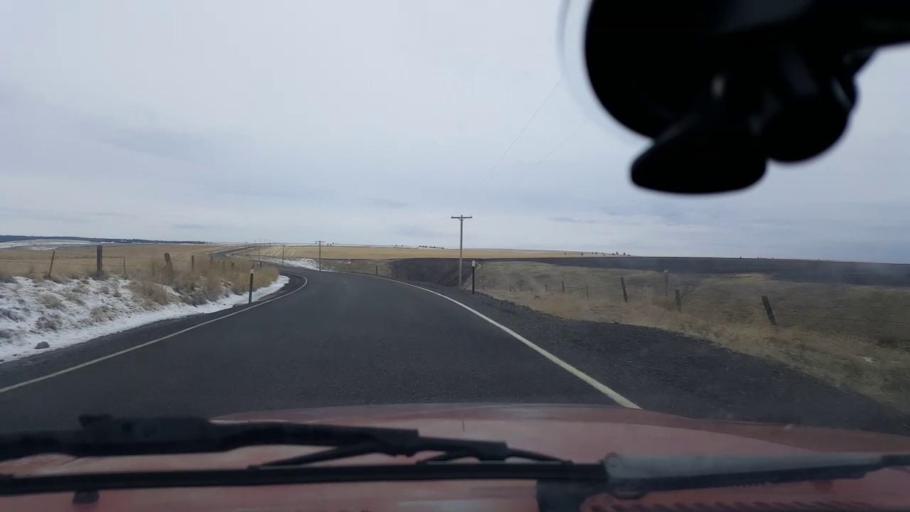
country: US
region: Washington
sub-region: Garfield County
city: Pomeroy
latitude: 46.3239
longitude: -117.3654
